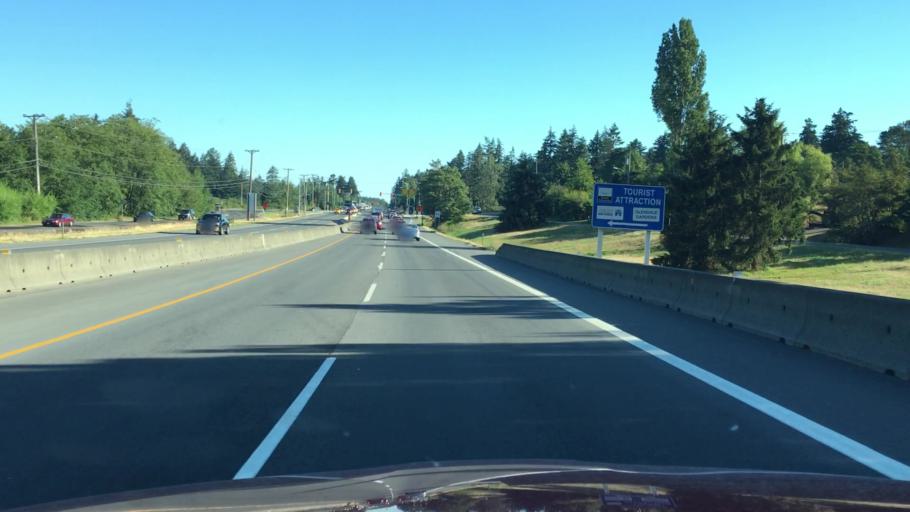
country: CA
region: British Columbia
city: Victoria
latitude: 48.5117
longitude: -123.3837
